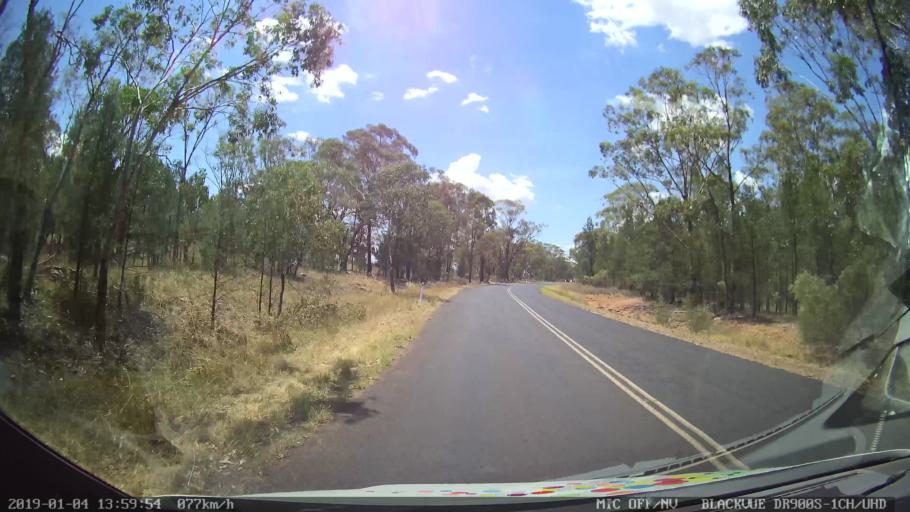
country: AU
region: New South Wales
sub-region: Dubbo Municipality
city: Dubbo
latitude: -32.3117
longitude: 148.5890
